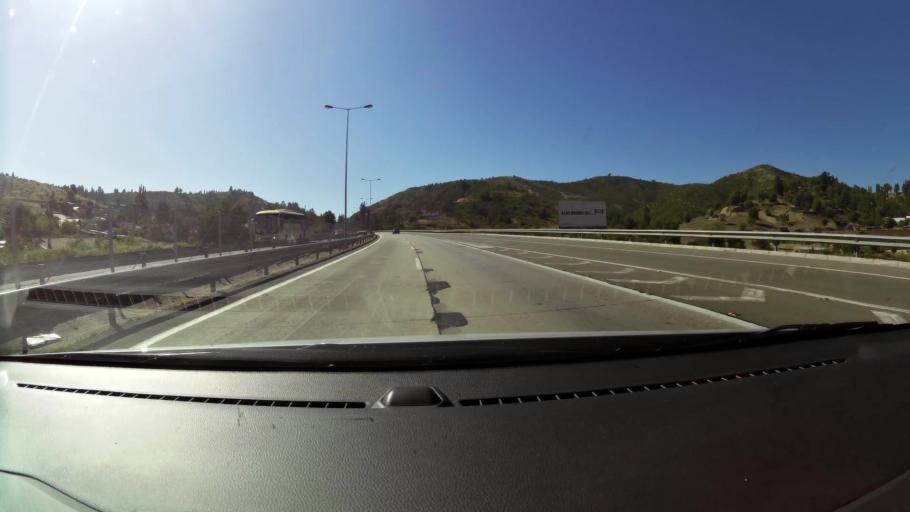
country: CL
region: Valparaiso
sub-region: Provincia de Marga Marga
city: Quilpue
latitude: -33.2426
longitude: -71.4510
